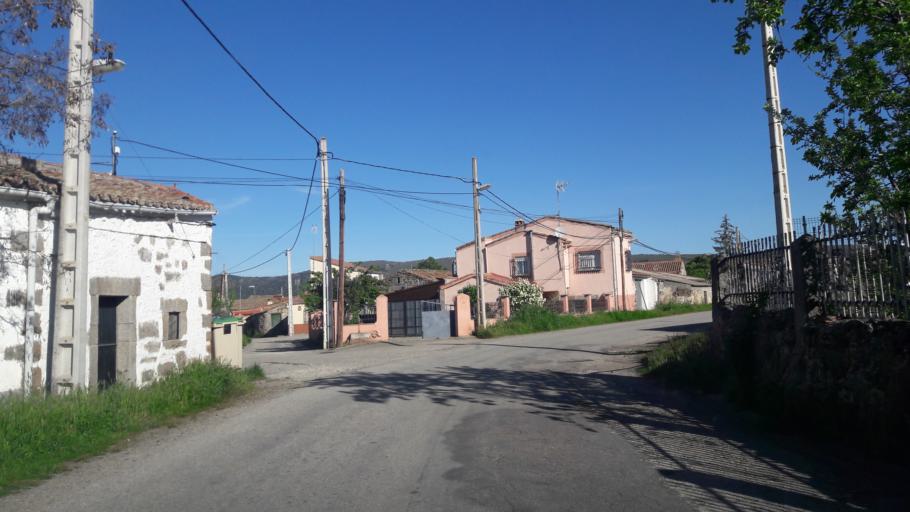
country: ES
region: Castille and Leon
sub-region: Provincia de Avila
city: Narrillos del Alamo
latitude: 40.5381
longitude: -5.4490
